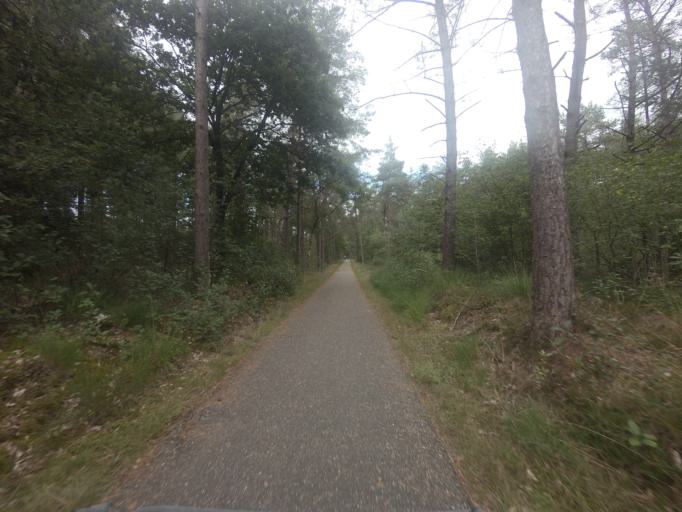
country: NL
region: Friesland
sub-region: Gemeente Weststellingwerf
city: Noordwolde
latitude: 52.9015
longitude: 6.2415
